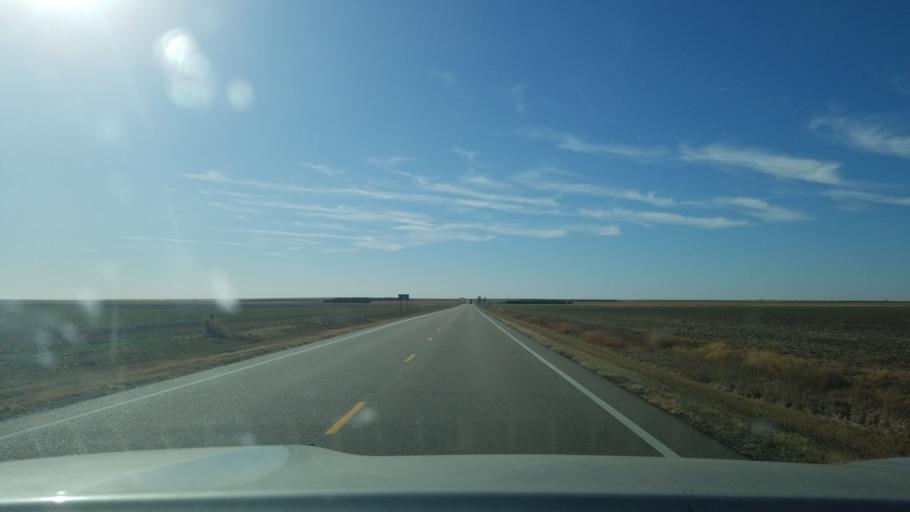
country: US
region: Kansas
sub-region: Ness County
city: Ness City
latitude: 38.3780
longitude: -99.8980
